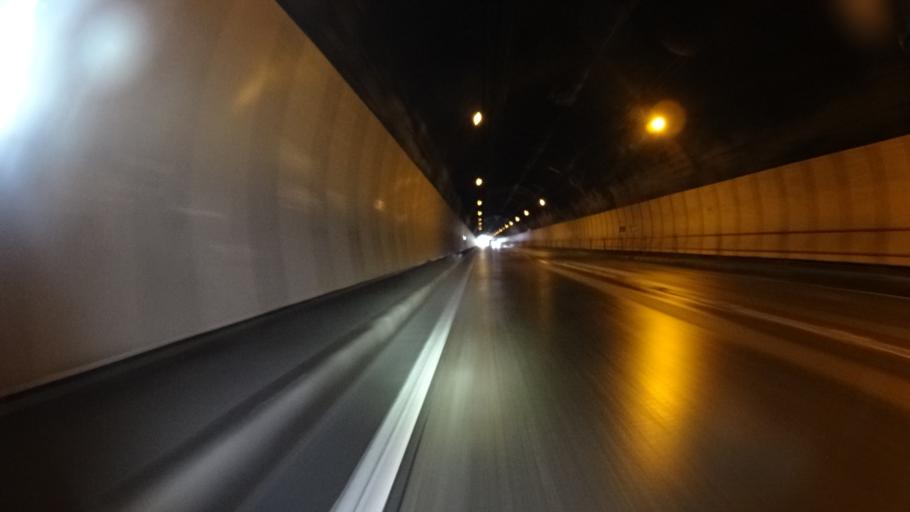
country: JP
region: Tokyo
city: Ome
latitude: 35.8173
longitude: 139.2465
